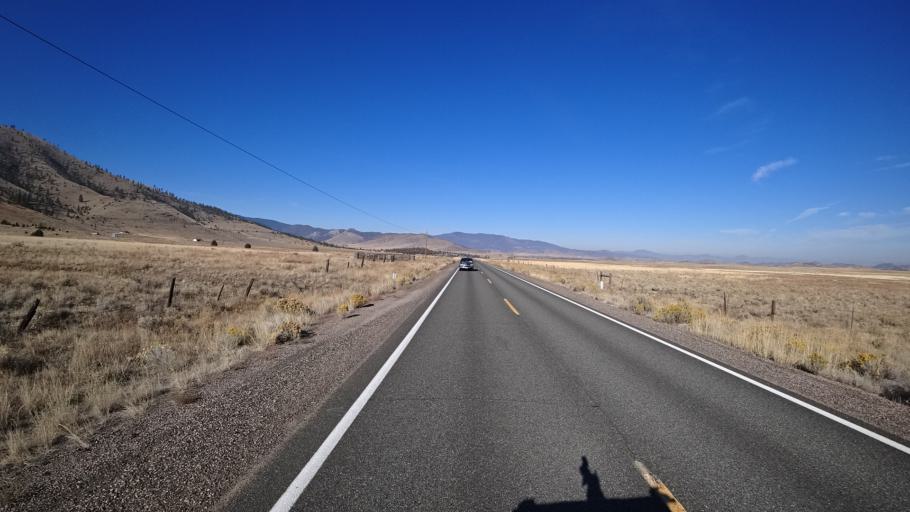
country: US
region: California
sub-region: Siskiyou County
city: Weed
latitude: 41.4805
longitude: -122.4944
